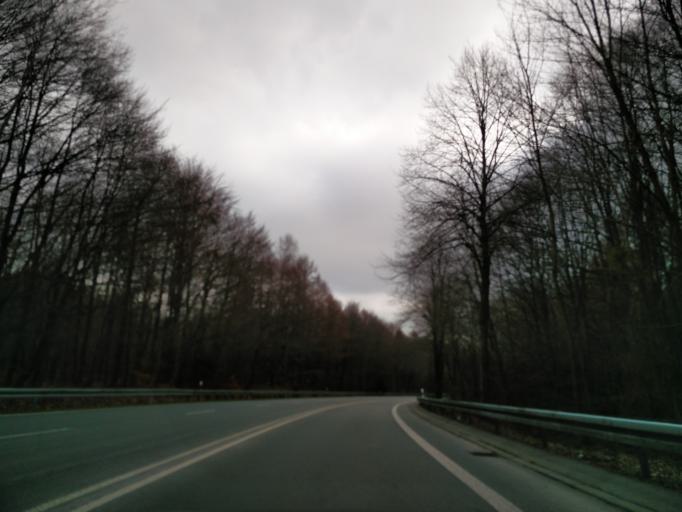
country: DE
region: North Rhine-Westphalia
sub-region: Regierungsbezirk Detmold
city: Willebadessen
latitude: 51.5709
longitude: 9.0031
